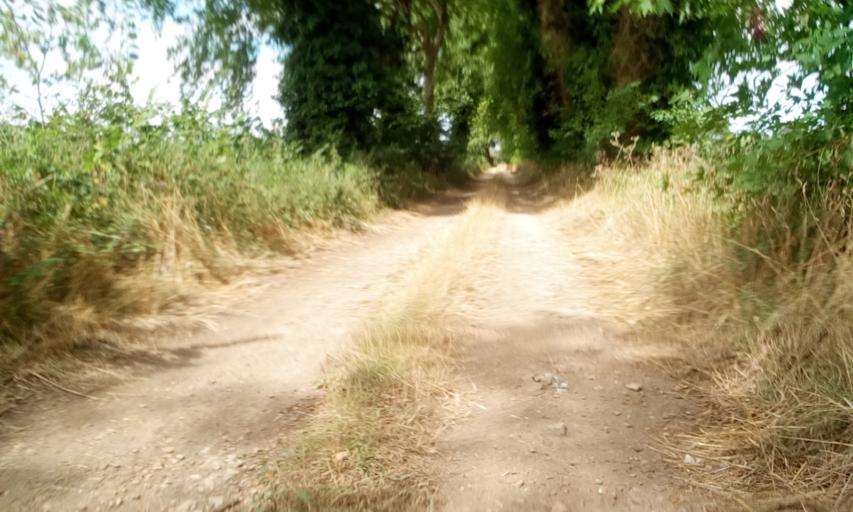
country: FR
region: Lower Normandy
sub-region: Departement du Calvados
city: Bellengreville
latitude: 49.1497
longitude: -0.2084
